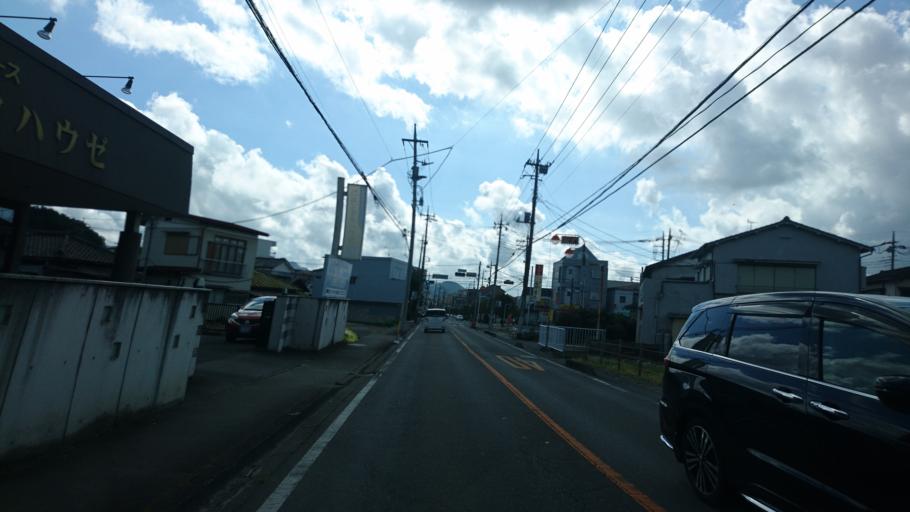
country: JP
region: Gunma
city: Kiryu
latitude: 36.4144
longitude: 139.3273
